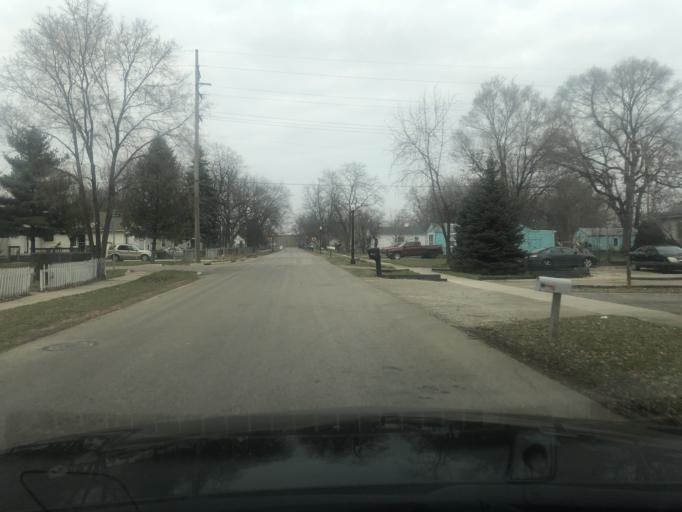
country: US
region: Michigan
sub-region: Wayne County
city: Belleville
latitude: 42.2152
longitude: -83.5492
